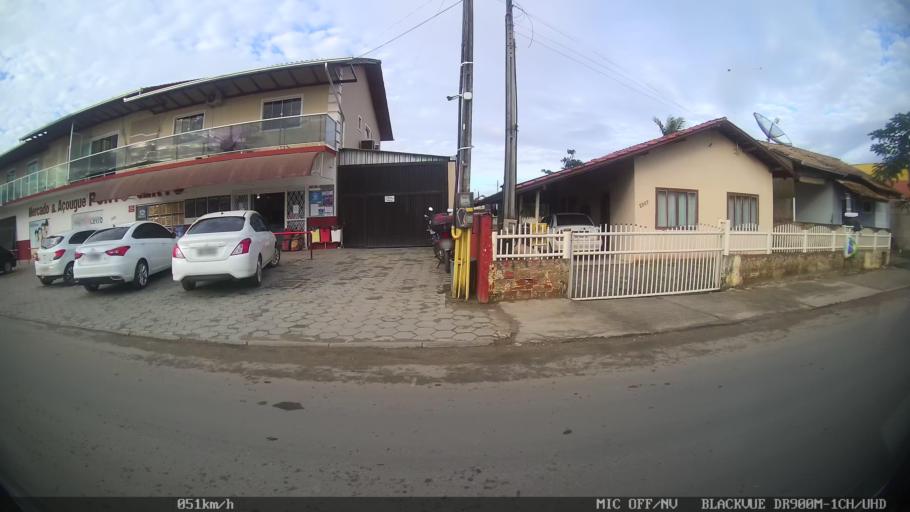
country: BR
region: Santa Catarina
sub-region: Barra Velha
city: Barra Velha
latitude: -26.6211
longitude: -48.7076
